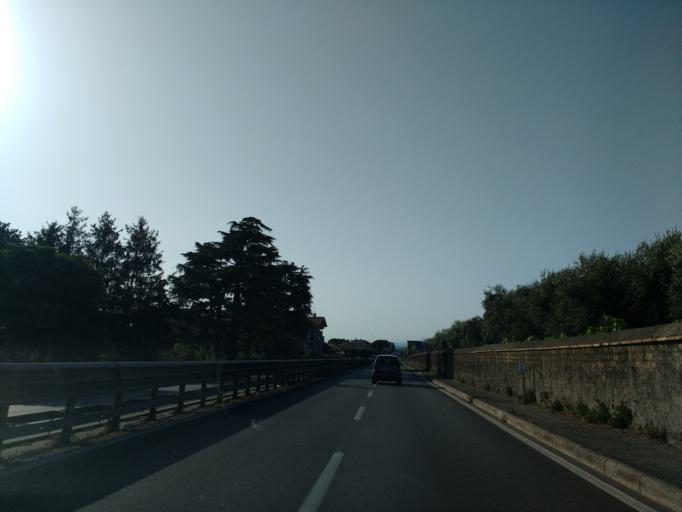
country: IT
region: Latium
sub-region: Citta metropolitana di Roma Capitale
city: Marino
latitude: 41.7631
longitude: 12.6205
